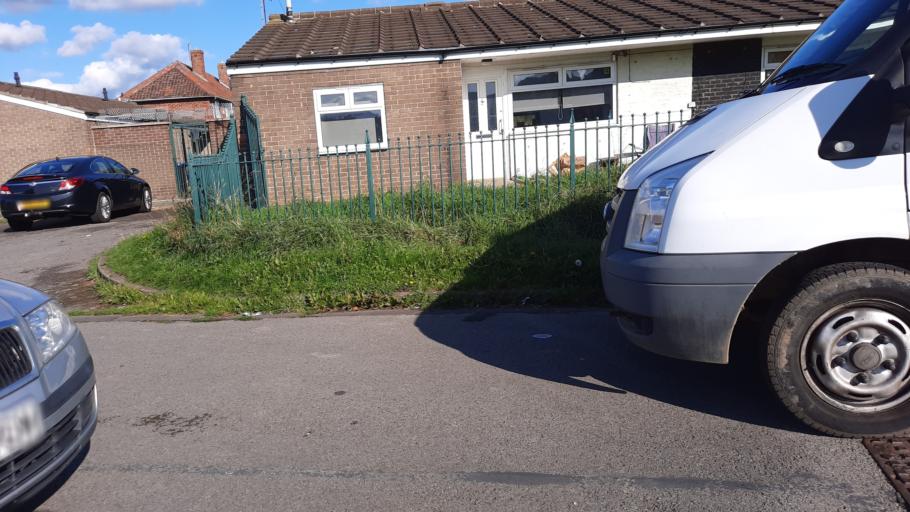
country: GB
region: England
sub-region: Redcar and Cleveland
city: South Bank
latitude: 54.5581
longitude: -1.1764
